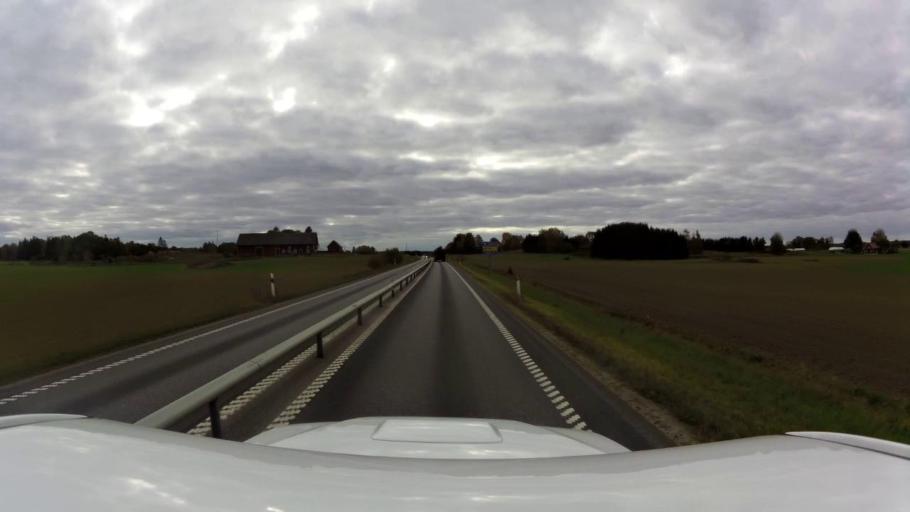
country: SE
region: OEstergoetland
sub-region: Linkopings Kommun
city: Malmslatt
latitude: 58.3379
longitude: 15.5561
